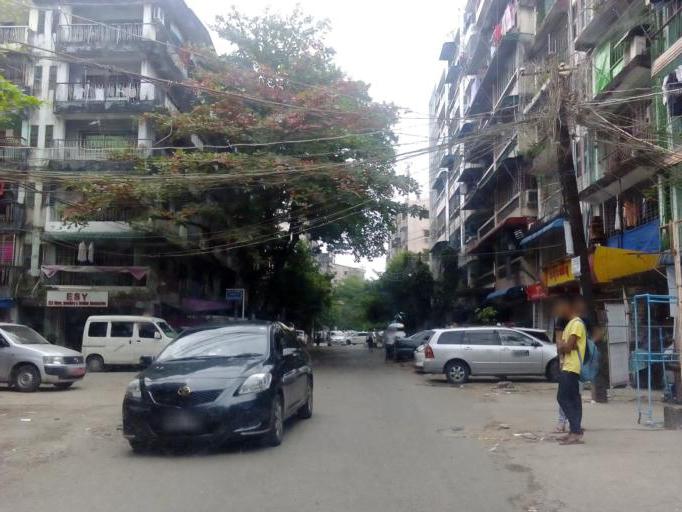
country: MM
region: Yangon
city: Yangon
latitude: 16.8037
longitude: 96.1764
